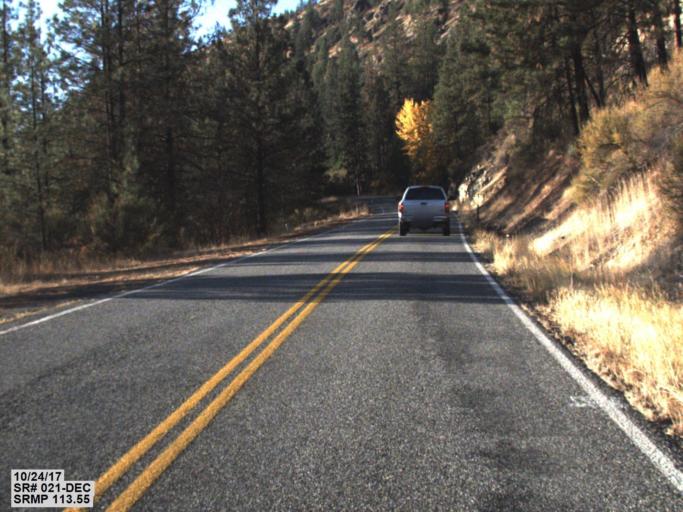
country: US
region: Washington
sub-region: Okanogan County
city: Coulee Dam
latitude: 48.0367
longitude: -118.6730
